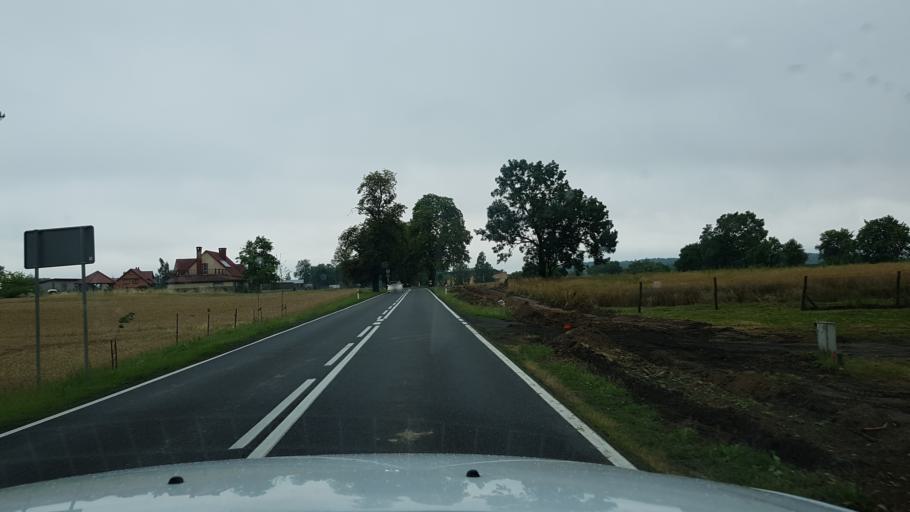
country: PL
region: West Pomeranian Voivodeship
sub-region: Powiat mysliborski
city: Mysliborz
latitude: 52.9226
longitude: 14.8427
